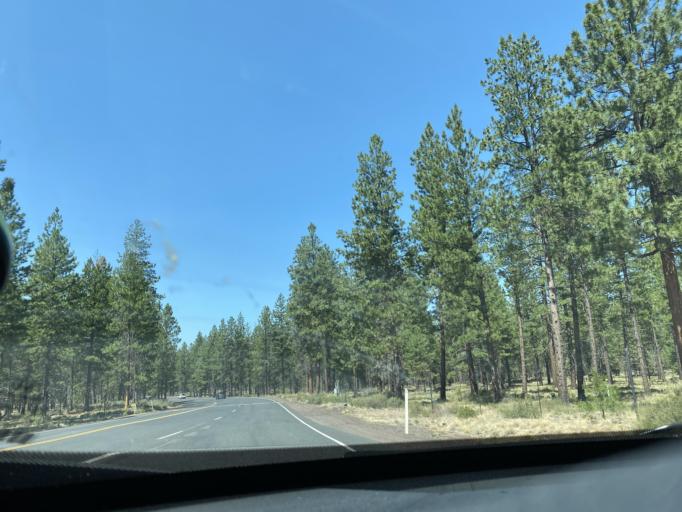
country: US
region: Oregon
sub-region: Deschutes County
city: Sunriver
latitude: 43.8908
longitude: -121.3832
